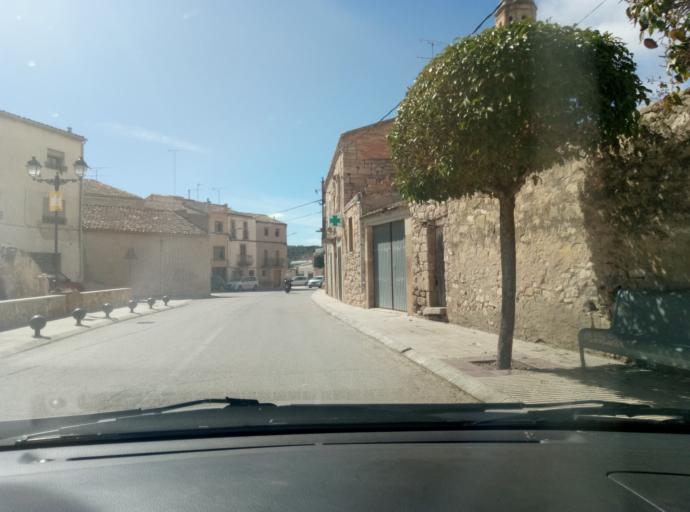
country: ES
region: Catalonia
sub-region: Provincia de Lleida
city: Vallbona de les Monges
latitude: 41.5599
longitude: 1.0552
